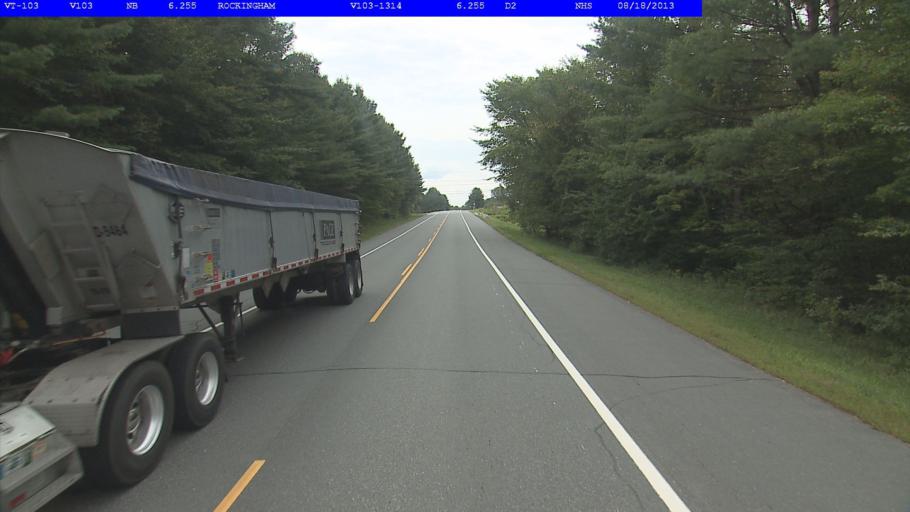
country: US
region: Vermont
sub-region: Windsor County
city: Chester
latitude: 43.2300
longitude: -72.5463
